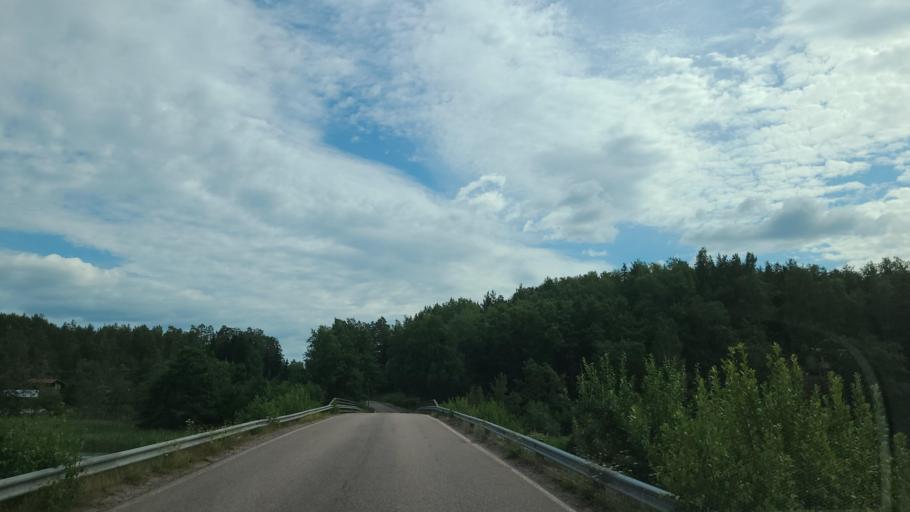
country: FI
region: Varsinais-Suomi
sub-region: Turku
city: Rymaettylae
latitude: 60.3414
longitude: 21.9779
